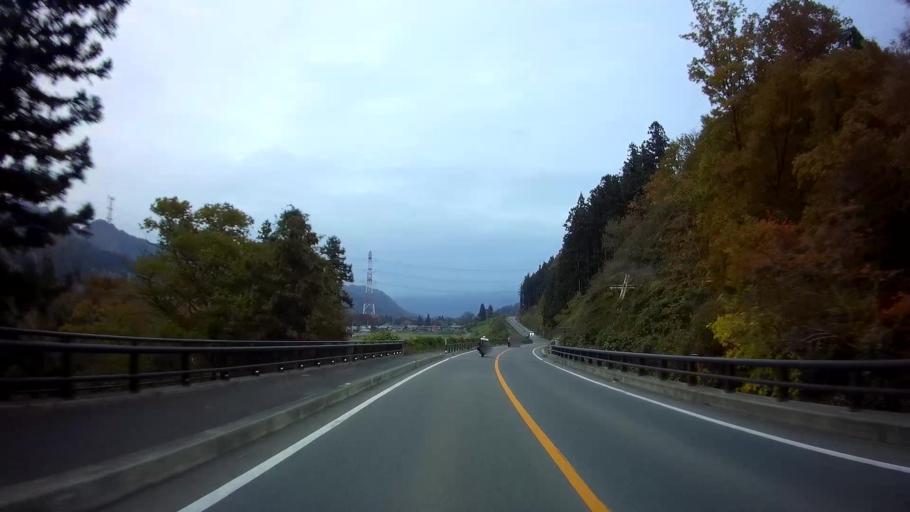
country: JP
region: Gunma
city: Nakanojomachi
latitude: 36.5649
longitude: 138.7464
